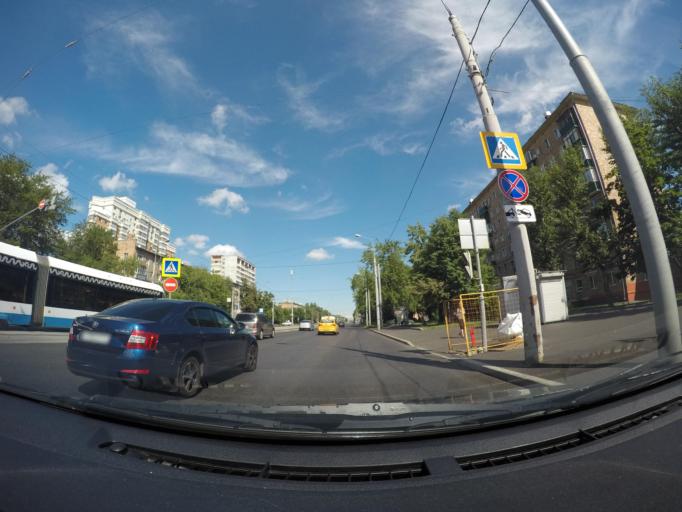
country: RU
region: Moscow
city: Lefortovo
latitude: 55.7632
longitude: 37.7347
